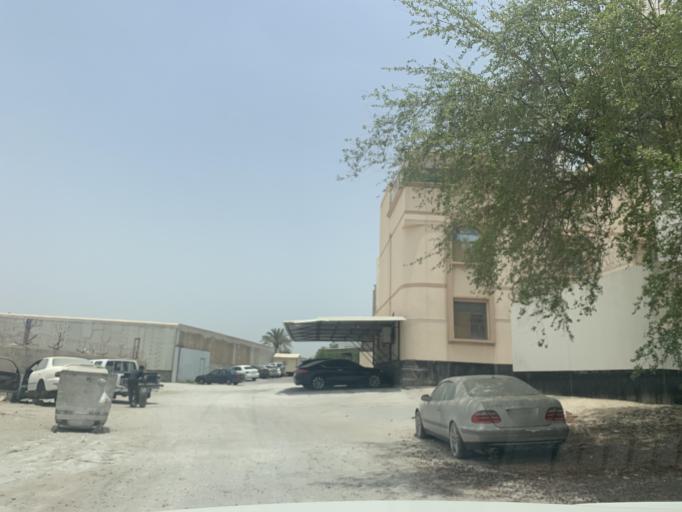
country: BH
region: Manama
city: Jidd Hafs
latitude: 26.2111
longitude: 50.5406
